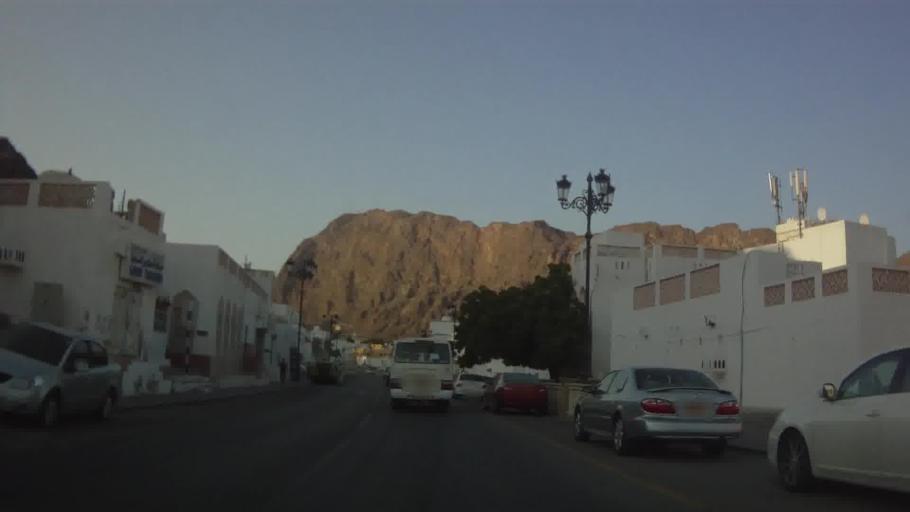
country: OM
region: Muhafazat Masqat
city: Muscat
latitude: 23.6017
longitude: 58.5975
